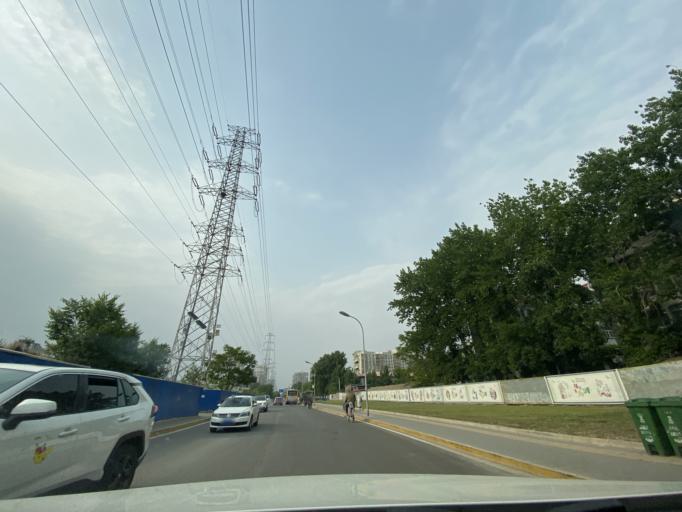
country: CN
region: Beijing
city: Haidian
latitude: 39.9818
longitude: 116.3347
